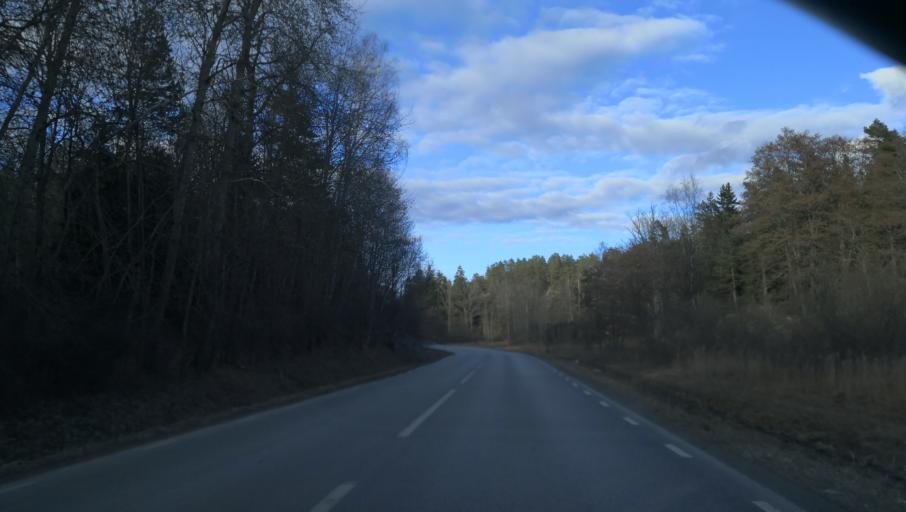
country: SE
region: Stockholm
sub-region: Varmdo Kommun
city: Gustavsberg
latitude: 59.3394
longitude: 18.3552
